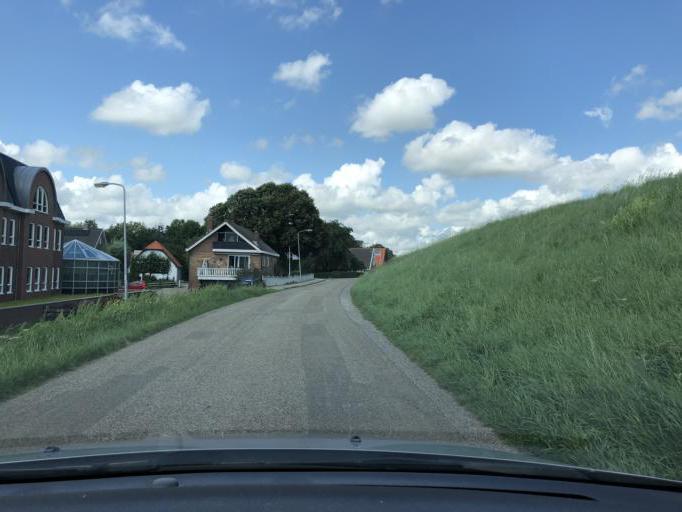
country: NL
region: North Holland
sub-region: Gemeente Hoorn
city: Hoorn
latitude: 52.6221
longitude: 5.0151
